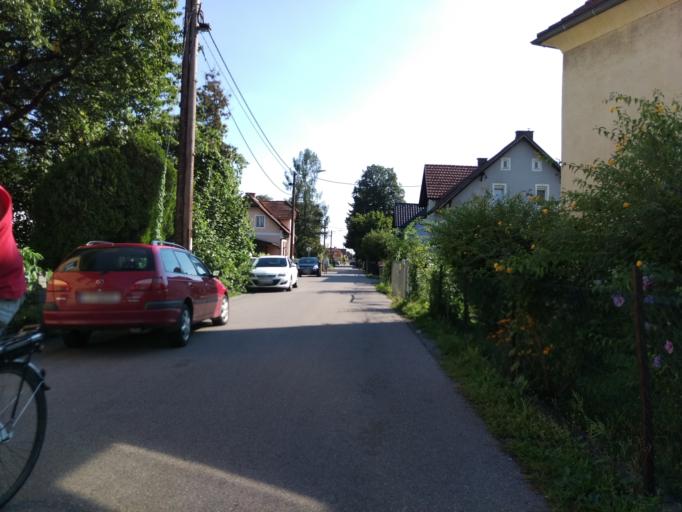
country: AT
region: Styria
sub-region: Politischer Bezirk Graz-Umgebung
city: Feldkirchen bei Graz
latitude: 47.0253
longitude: 15.4297
